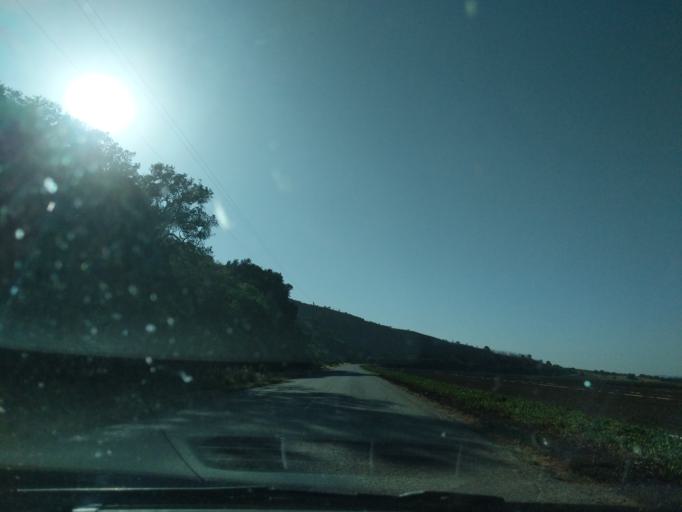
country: US
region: California
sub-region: Monterey County
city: Soledad
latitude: 36.4133
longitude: -121.3932
